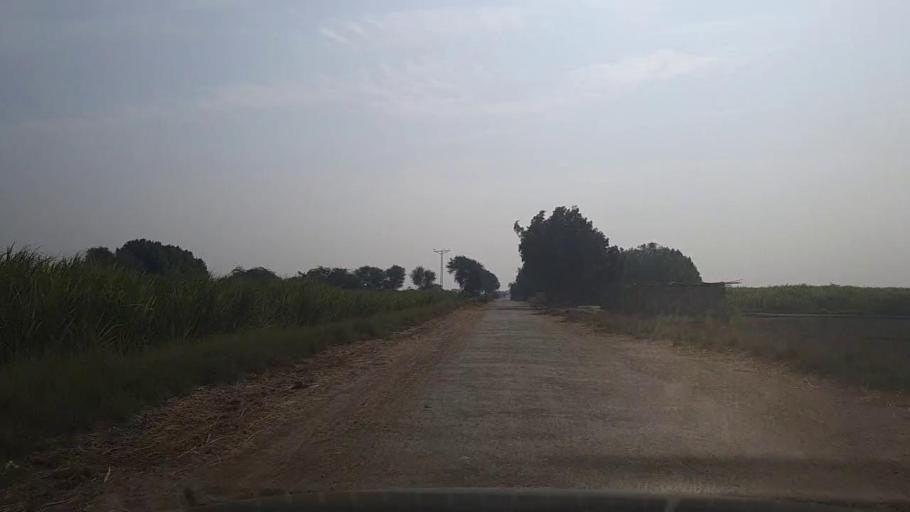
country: PK
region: Sindh
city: Bulri
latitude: 25.0065
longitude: 68.3017
